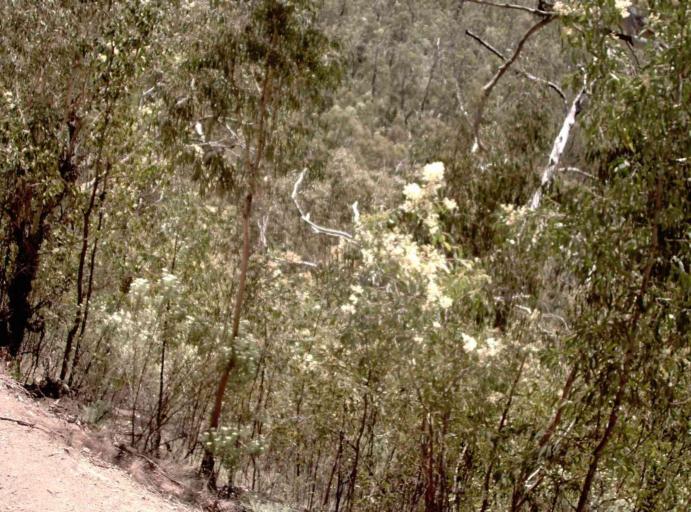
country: AU
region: New South Wales
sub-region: Snowy River
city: Jindabyne
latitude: -37.0027
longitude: 148.2953
